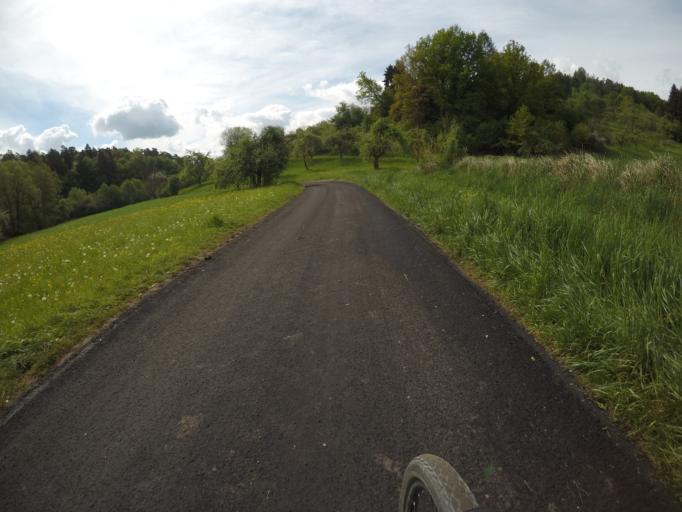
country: DE
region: Baden-Wuerttemberg
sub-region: Tuebingen Region
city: Tuebingen
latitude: 48.5314
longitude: 9.0055
